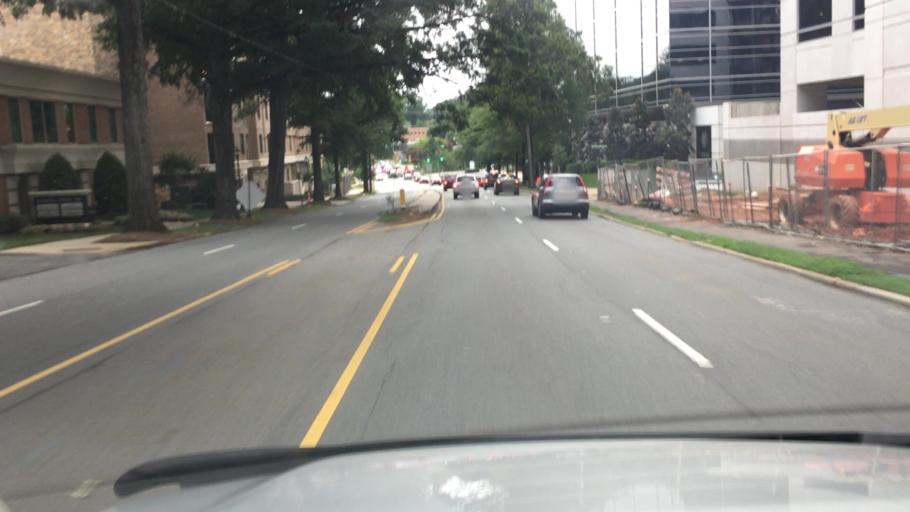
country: US
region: North Carolina
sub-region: Mecklenburg County
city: Charlotte
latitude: 35.2072
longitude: -80.8386
